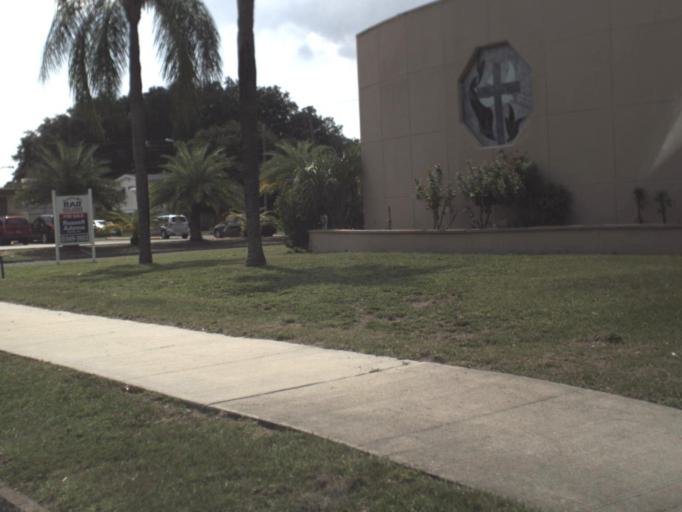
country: US
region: Florida
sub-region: Pinellas County
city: Saint Petersburg
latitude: 27.7772
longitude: -82.6867
